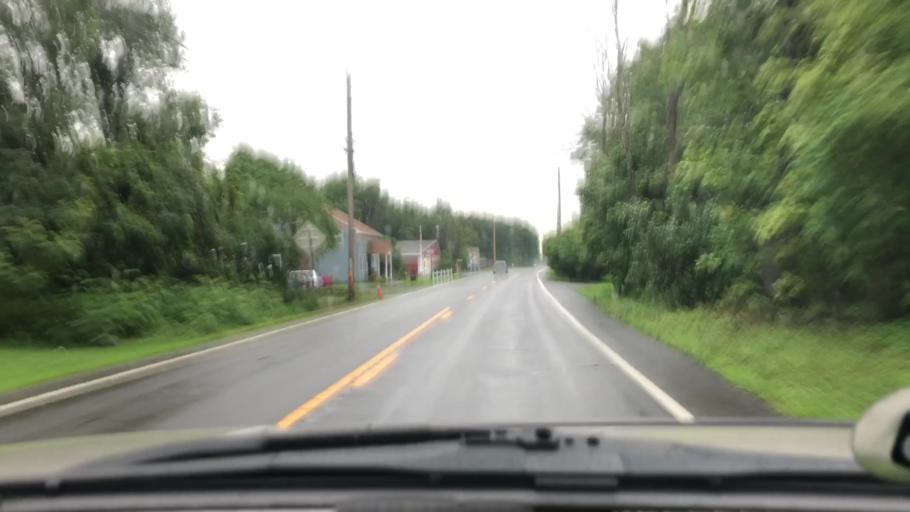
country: US
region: New York
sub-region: Greene County
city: Palenville
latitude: 42.1467
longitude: -74.0022
